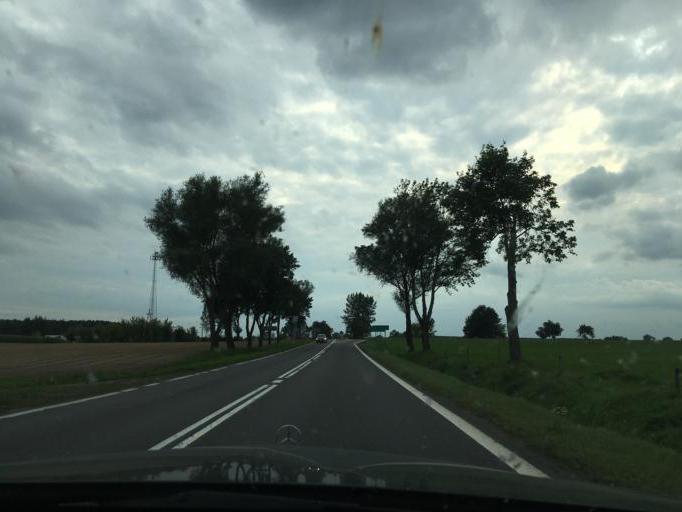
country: PL
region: Podlasie
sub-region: Powiat kolnenski
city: Stawiski
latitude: 53.4681
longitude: 22.2028
